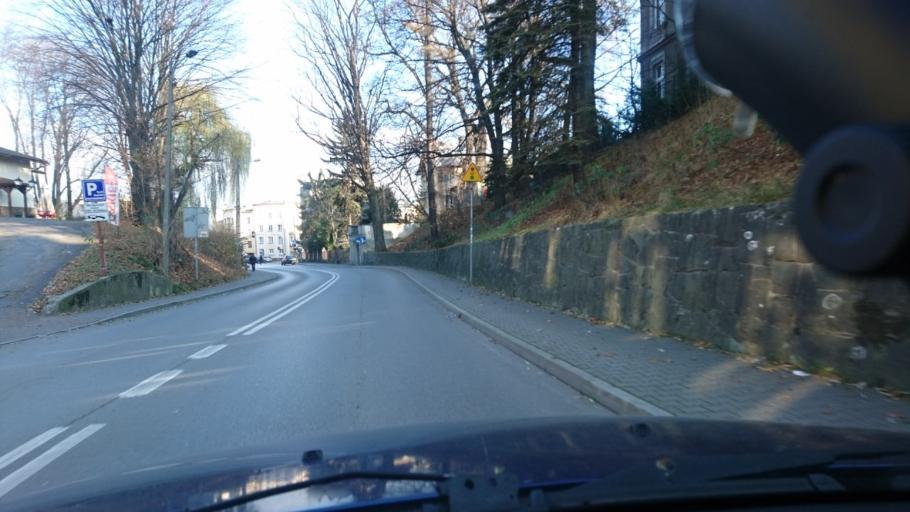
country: PL
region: Silesian Voivodeship
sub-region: Powiat cieszynski
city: Cieszyn
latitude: 49.7488
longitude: 18.6372
